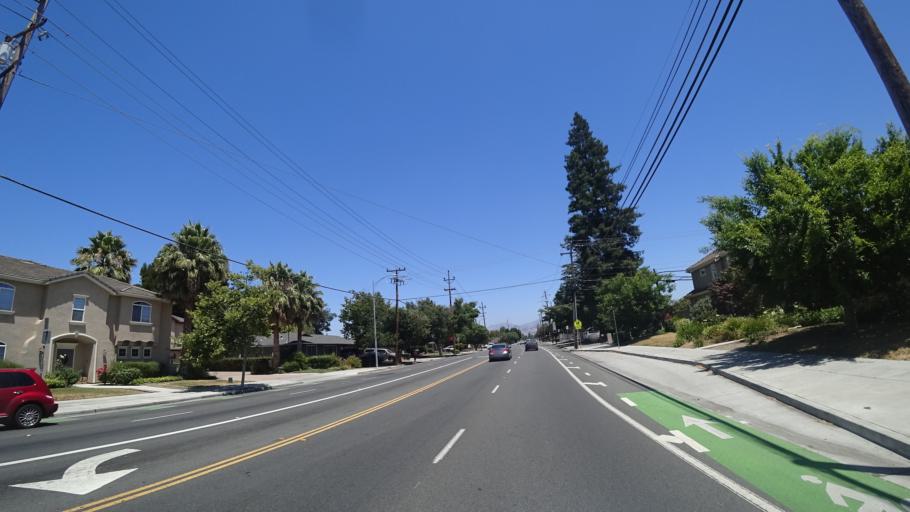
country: US
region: California
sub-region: Santa Clara County
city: Cambrian Park
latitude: 37.2607
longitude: -121.8852
